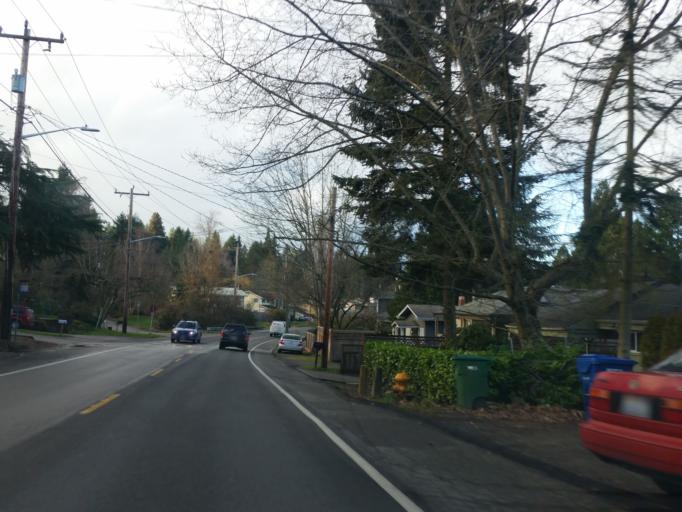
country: US
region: Washington
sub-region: King County
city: Inglewood-Finn Hill
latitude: 47.6937
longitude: -122.2737
